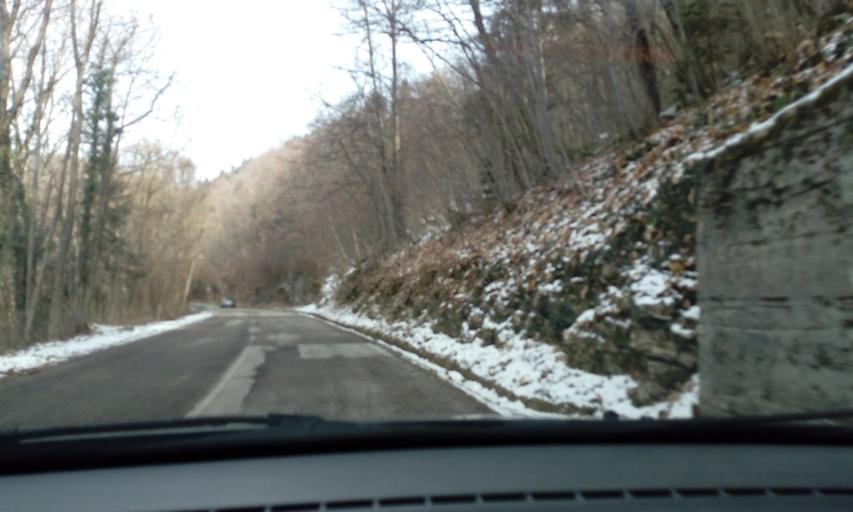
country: IT
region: Friuli Venezia Giulia
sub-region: Provincia di Udine
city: Savogna
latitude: 46.1777
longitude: 13.5573
